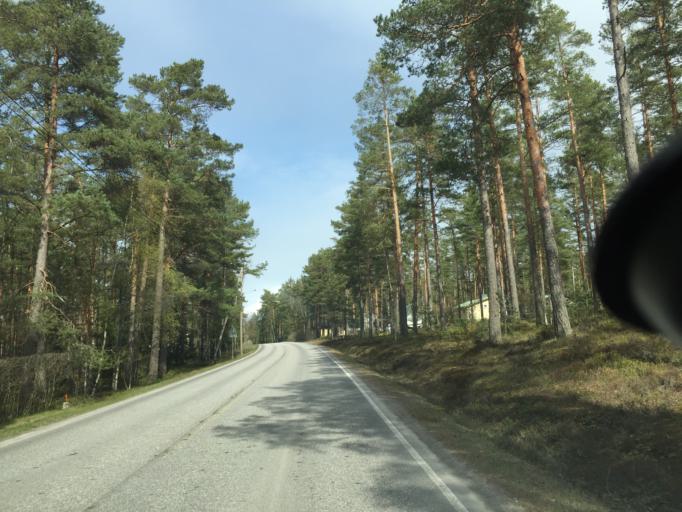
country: FI
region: Varsinais-Suomi
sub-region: Salo
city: Saerkisalo
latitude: 59.9790
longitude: 23.0116
